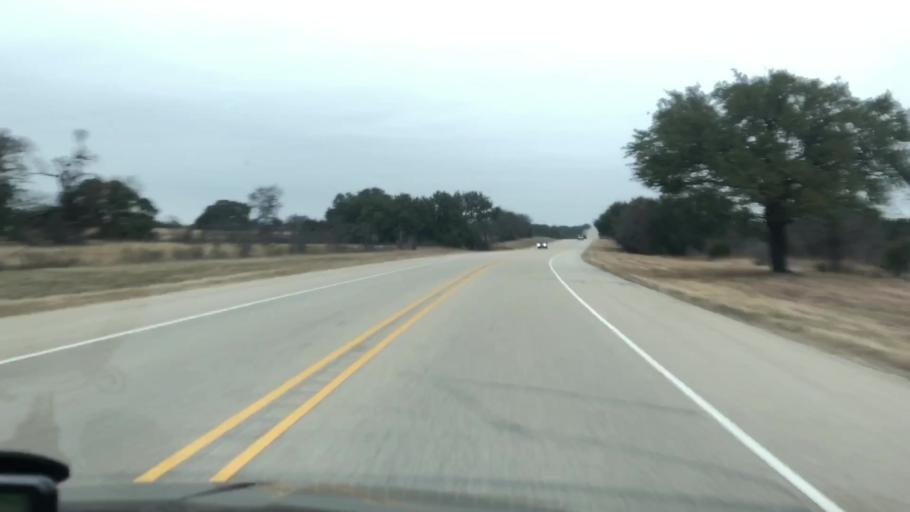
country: US
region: Texas
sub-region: Hamilton County
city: Hamilton
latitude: 31.5486
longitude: -98.1602
